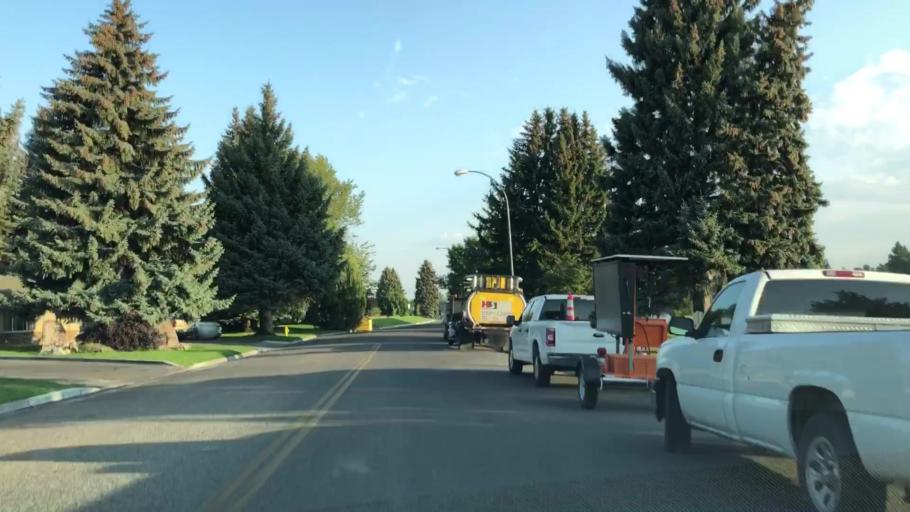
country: US
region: Idaho
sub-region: Bonneville County
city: Idaho Falls
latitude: 43.4983
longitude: -112.0443
